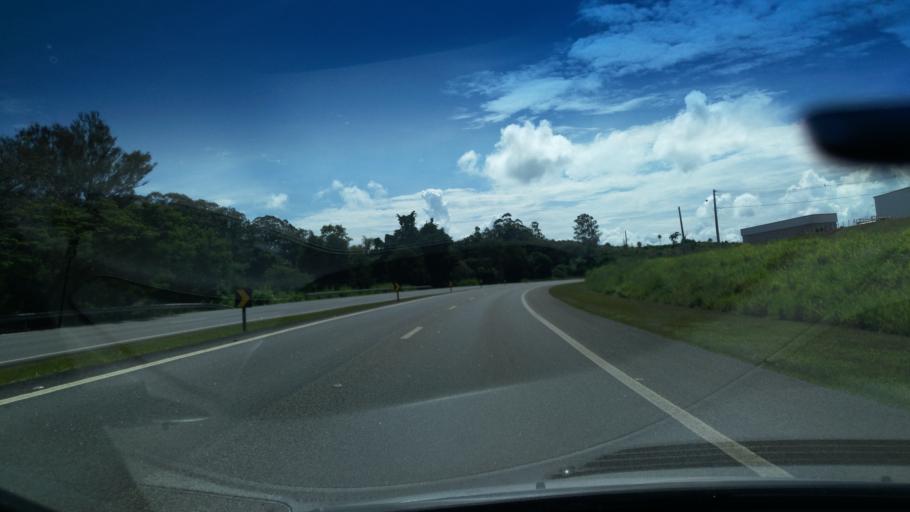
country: BR
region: Sao Paulo
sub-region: Santo Antonio Do Jardim
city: Espirito Santo do Pinhal
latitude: -22.2245
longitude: -46.7932
